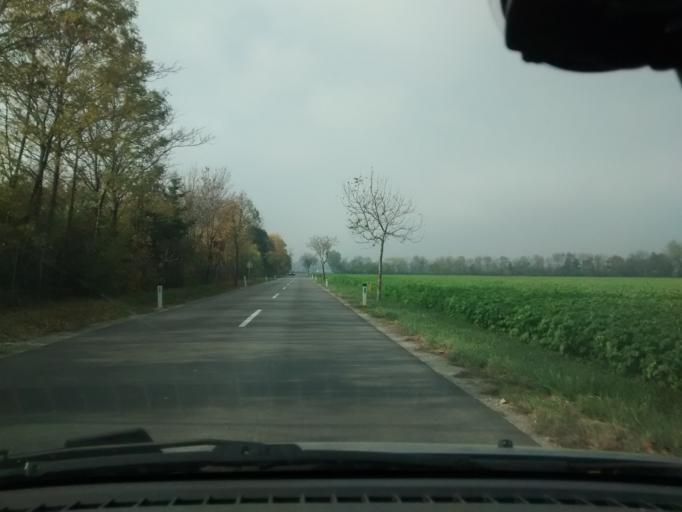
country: AT
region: Lower Austria
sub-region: Politischer Bezirk Modling
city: Munchendorf
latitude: 48.0306
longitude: 16.3520
